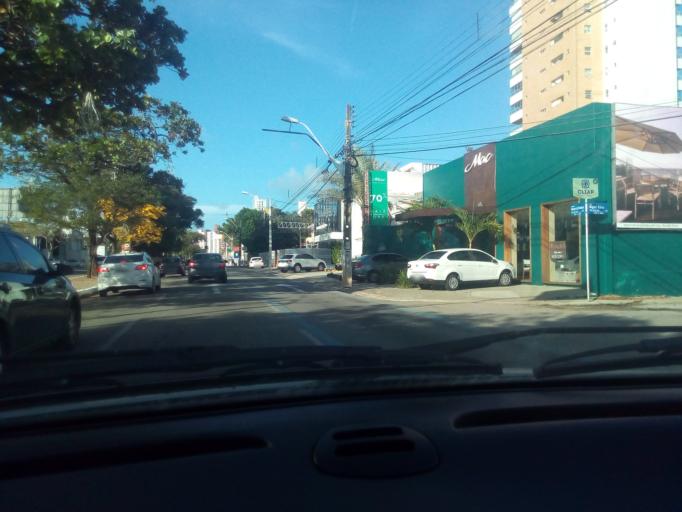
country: BR
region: Rio Grande do Norte
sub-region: Natal
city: Natal
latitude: -5.7941
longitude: -35.1982
